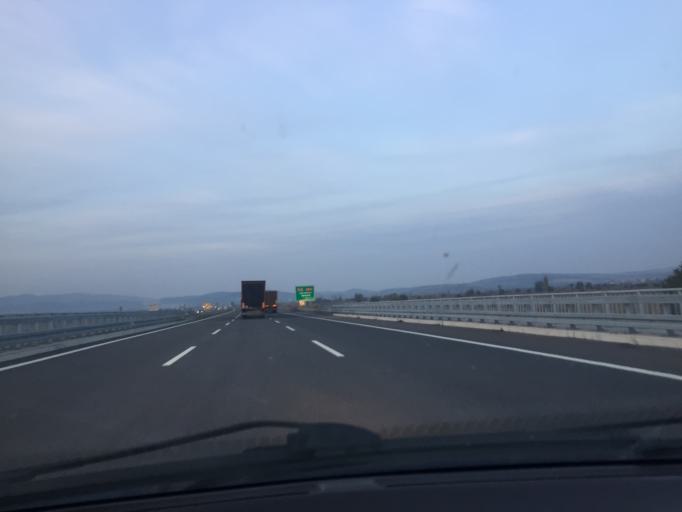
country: TR
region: Manisa
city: Halitpasa
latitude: 38.7449
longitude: 27.6591
